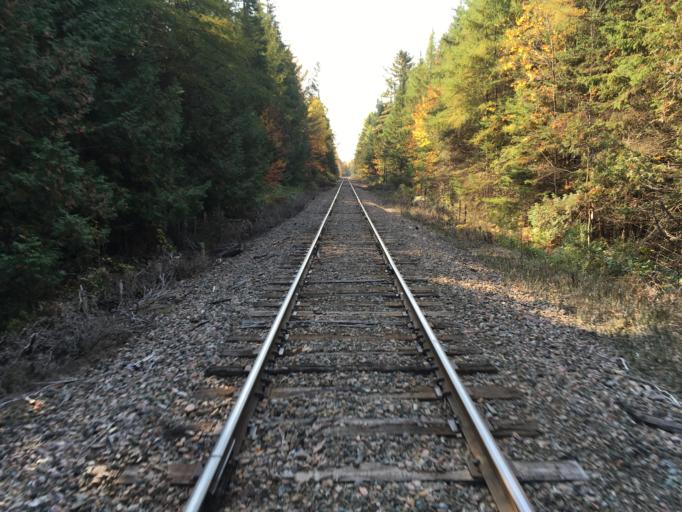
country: US
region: Vermont
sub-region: Caledonia County
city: Lyndonville
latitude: 44.6124
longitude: -71.9667
